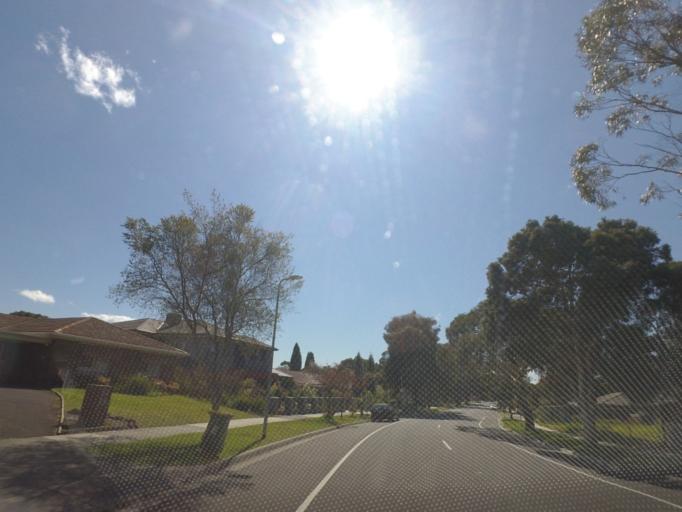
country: AU
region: Victoria
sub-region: Knox
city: Wantirna South
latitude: -37.8819
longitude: 145.2231
